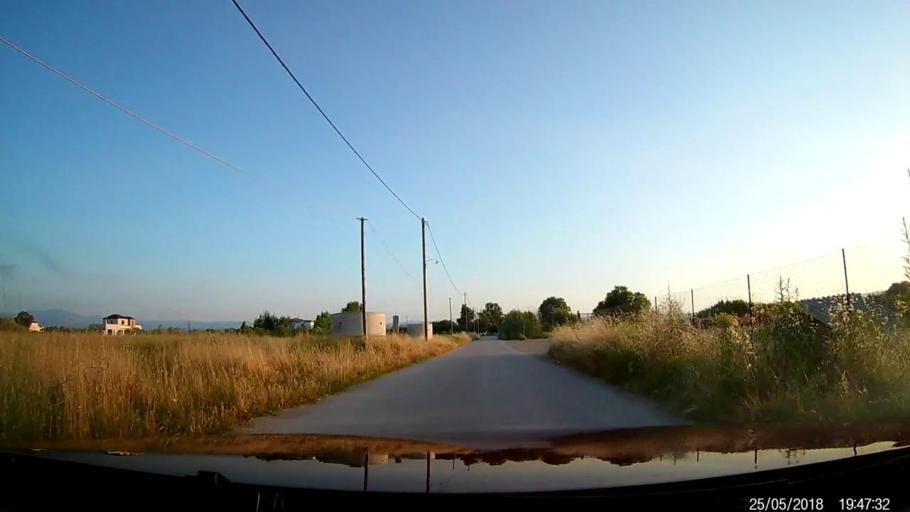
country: GR
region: Central Greece
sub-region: Nomos Evvoias
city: Ayios Nikolaos
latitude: 38.4218
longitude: 23.6375
